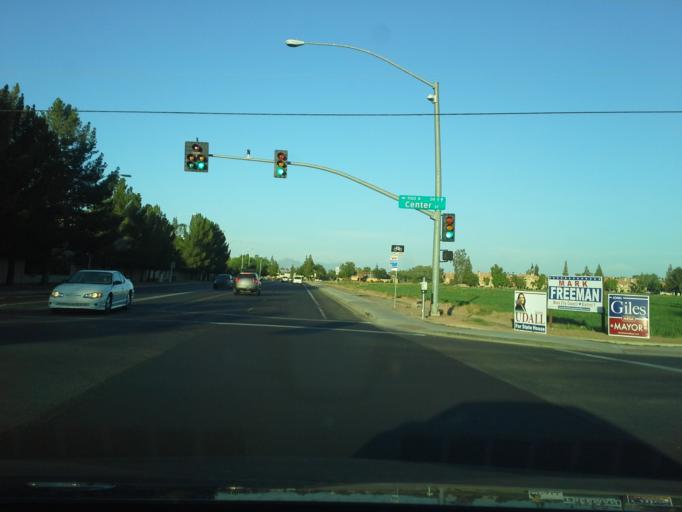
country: US
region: Arizona
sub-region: Maricopa County
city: Mesa
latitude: 33.4349
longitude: -111.8315
